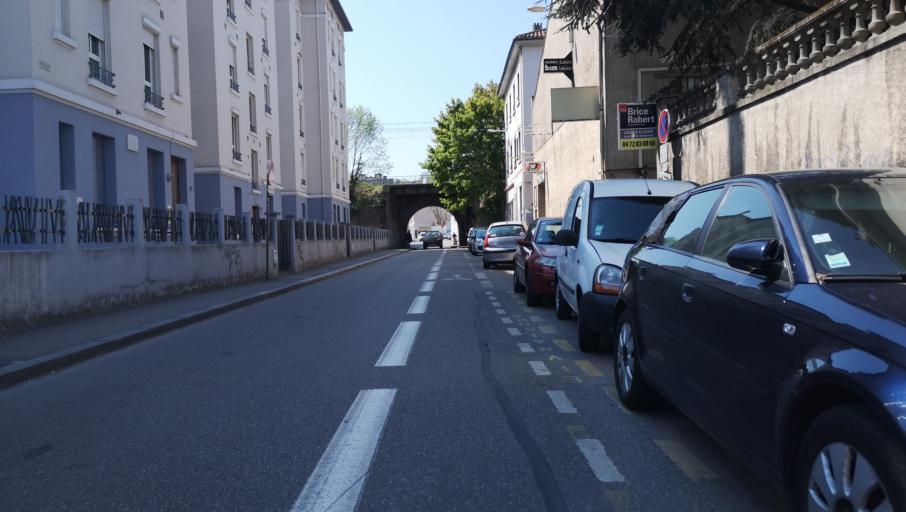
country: FR
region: Rhone-Alpes
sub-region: Departement du Rhone
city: Tassin-la-Demi-Lune
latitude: 45.7735
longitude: 4.7992
